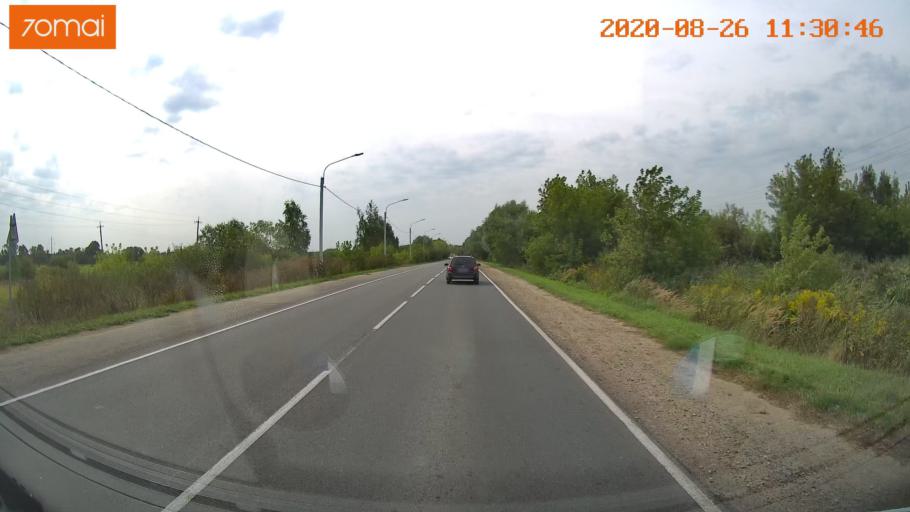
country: RU
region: Rjazan
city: Shilovo
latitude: 54.3129
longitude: 40.8791
